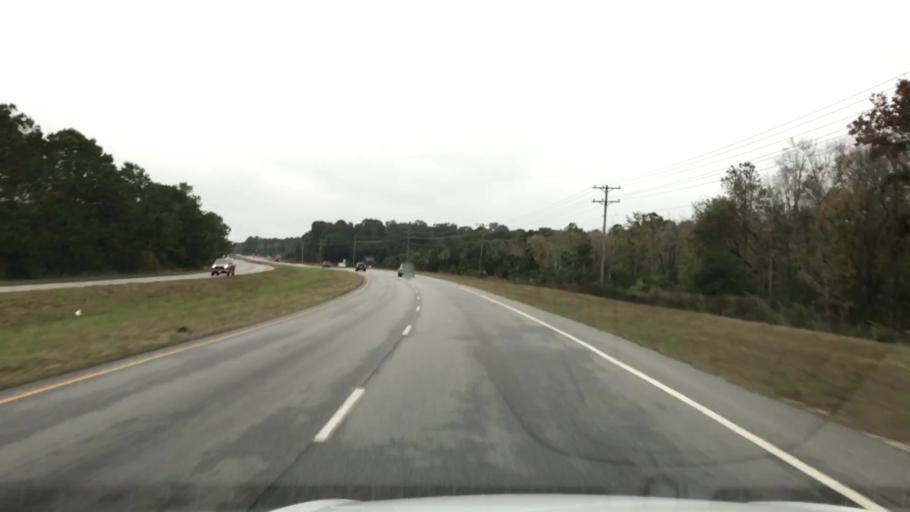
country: US
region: South Carolina
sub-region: Charleston County
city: Isle of Palms
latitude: 32.9184
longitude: -79.7166
